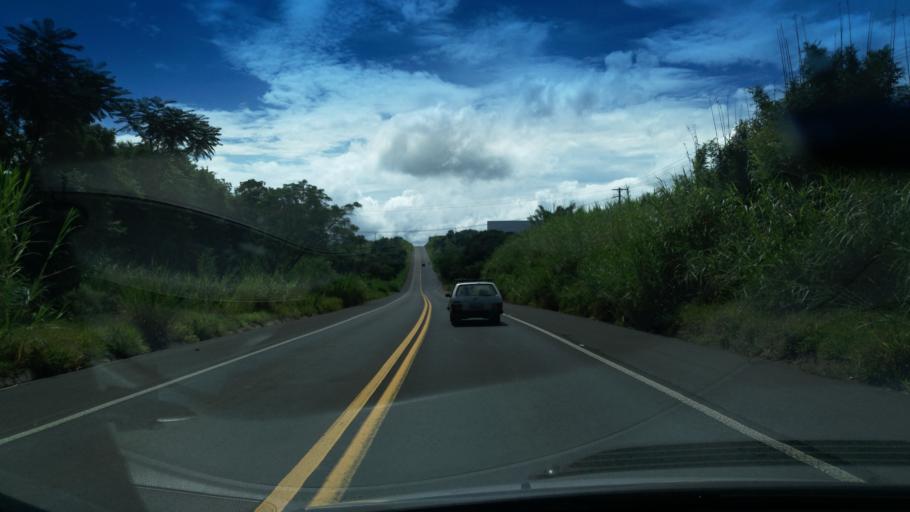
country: BR
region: Sao Paulo
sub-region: Santo Antonio Do Jardim
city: Espirito Santo do Pinhal
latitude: -22.1600
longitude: -46.7295
